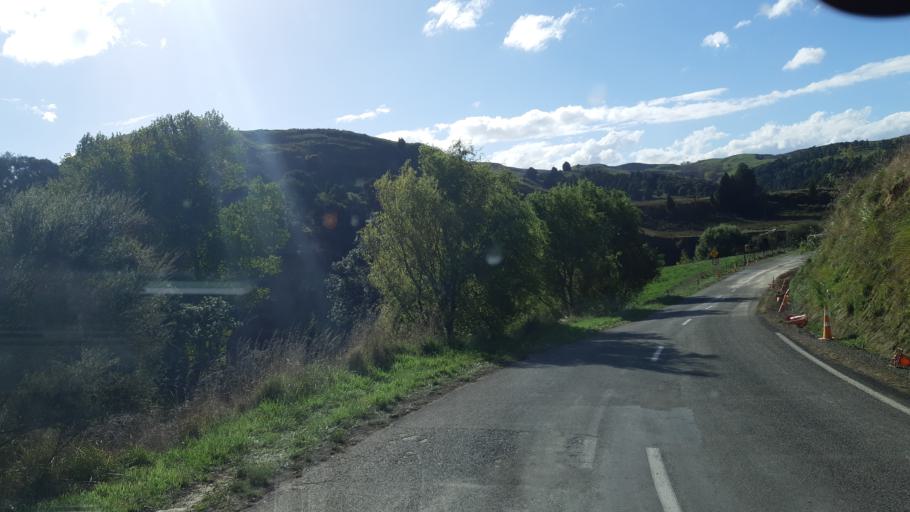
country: NZ
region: Manawatu-Wanganui
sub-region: Rangitikei District
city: Bulls
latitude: -39.9110
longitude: 175.3590
